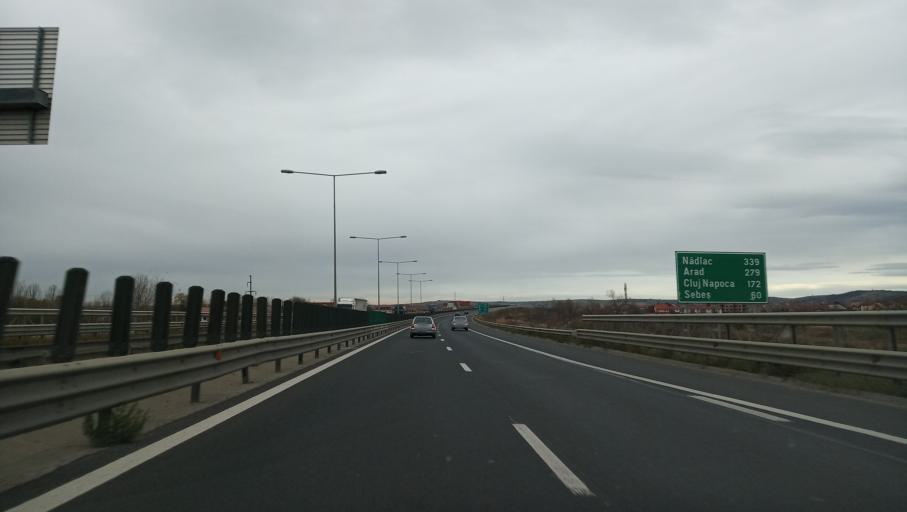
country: RO
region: Sibiu
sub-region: Municipiul Sibiu
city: Sibiu
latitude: 45.8037
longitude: 24.1820
